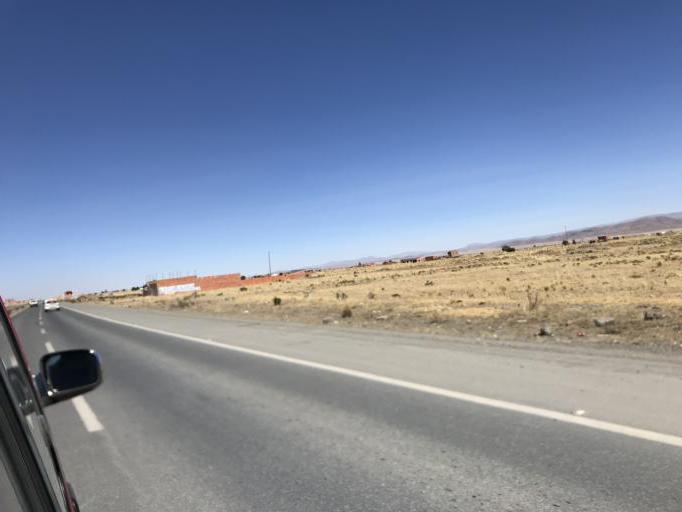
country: BO
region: La Paz
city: Batallas
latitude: -16.3420
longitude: -68.4095
